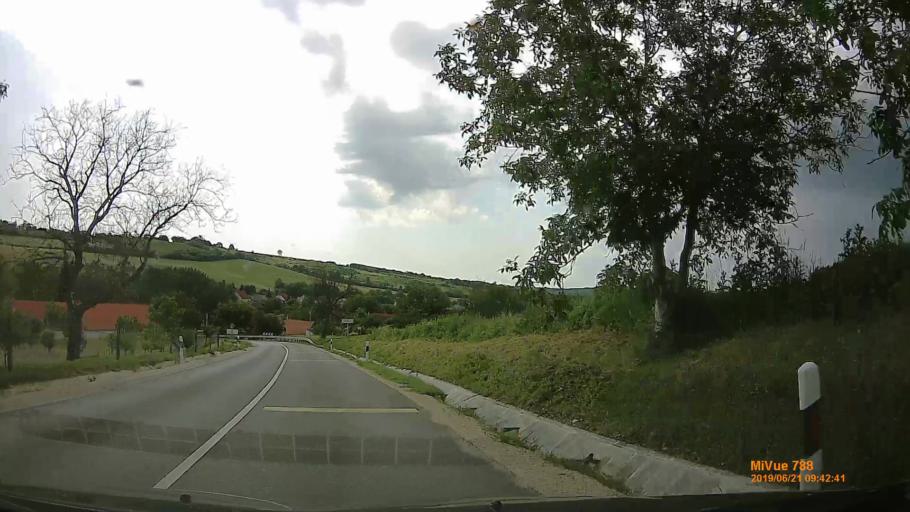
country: HU
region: Somogy
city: Taszar
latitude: 46.2864
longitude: 17.9698
